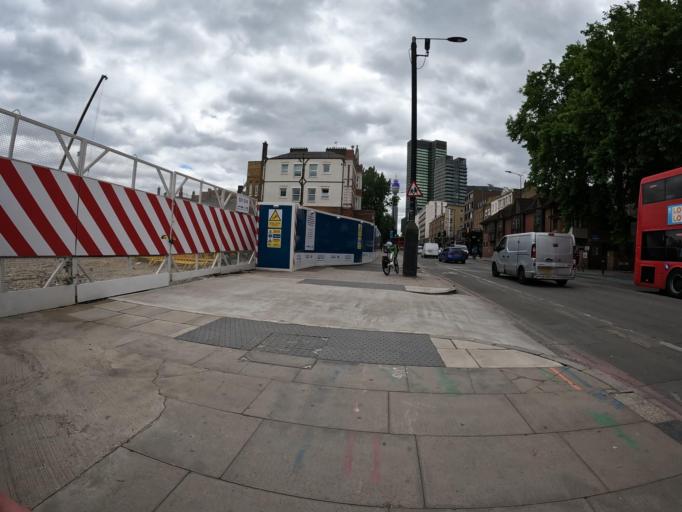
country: GB
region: England
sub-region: Greater London
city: Camden Town
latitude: 51.5286
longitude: -0.1384
